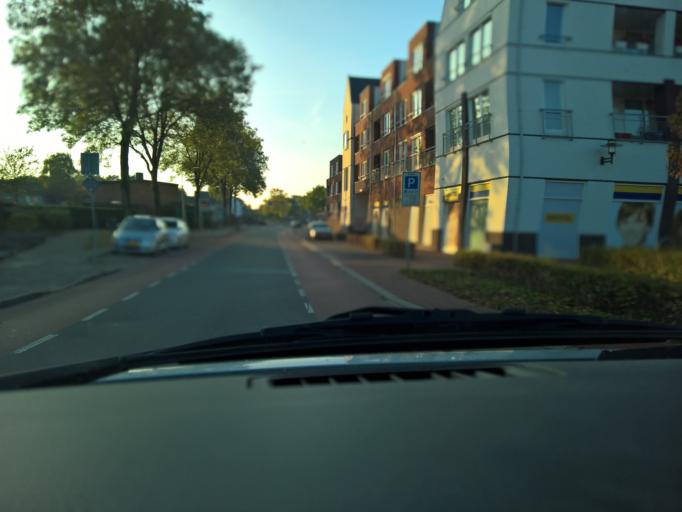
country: NL
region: Gelderland
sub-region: Gemeente Beuningen
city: Beuningen
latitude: 51.8593
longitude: 5.7706
